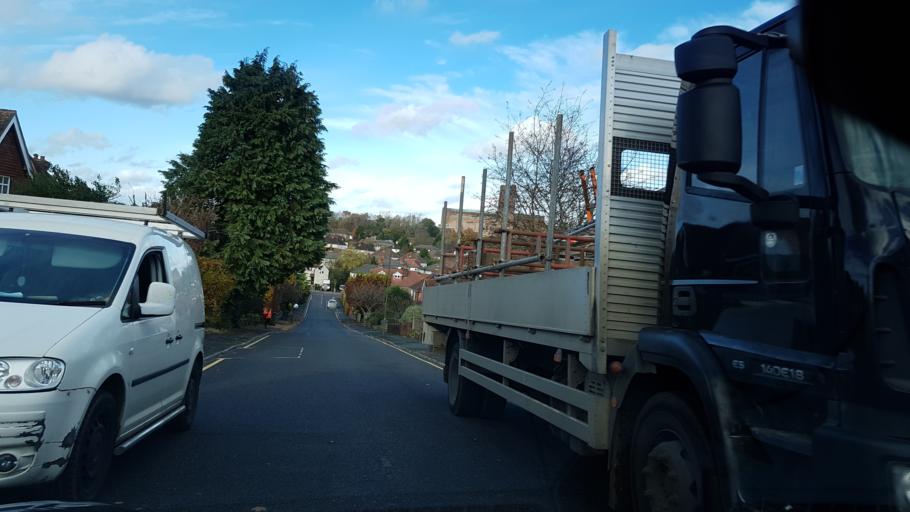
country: GB
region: England
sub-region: Surrey
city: Guildford
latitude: 51.2351
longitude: -0.5906
